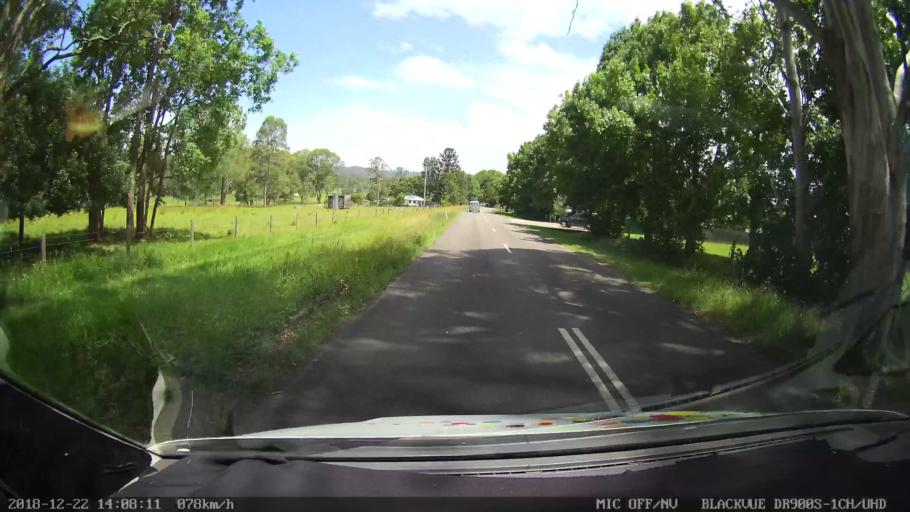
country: AU
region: New South Wales
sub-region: Clarence Valley
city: Coutts Crossing
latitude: -29.9757
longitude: 152.7259
